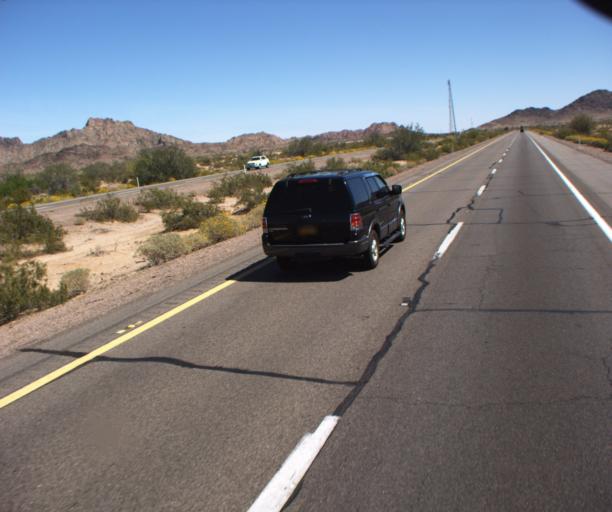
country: US
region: Arizona
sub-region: Yuma County
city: Wellton
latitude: 32.7206
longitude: -113.7738
